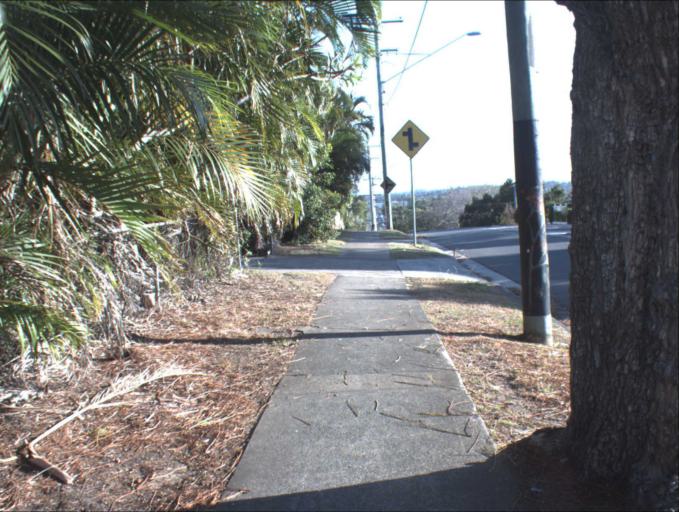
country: AU
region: Queensland
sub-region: Logan
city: Rochedale South
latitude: -27.5988
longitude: 153.1215
